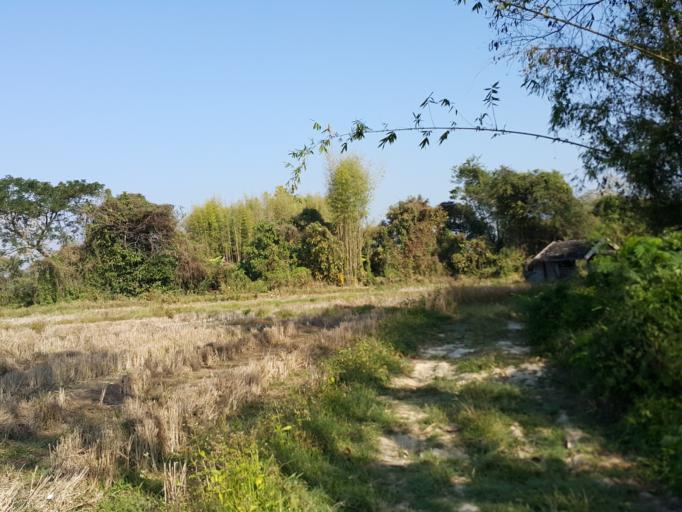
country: TH
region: Chiang Mai
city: San Kamphaeng
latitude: 18.8163
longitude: 99.1107
